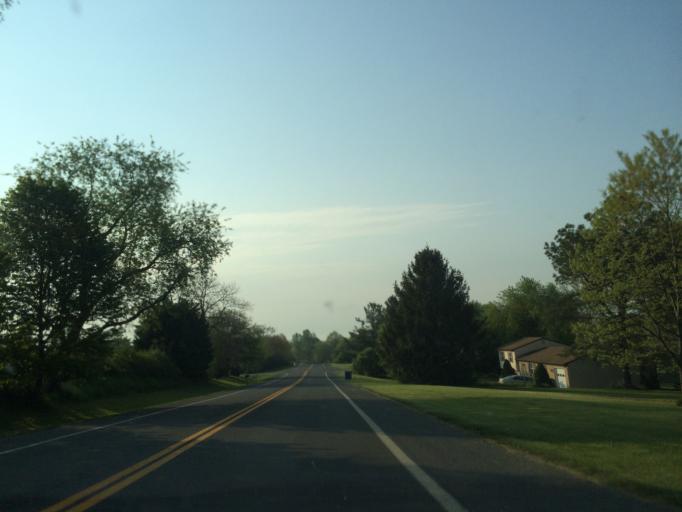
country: US
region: Maryland
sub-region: Carroll County
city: Sykesville
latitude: 39.3969
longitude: -77.0293
